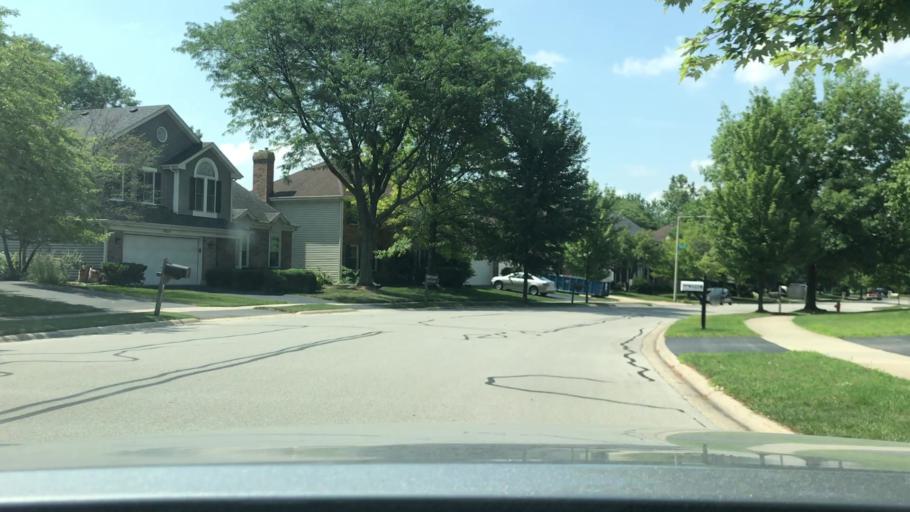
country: US
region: Illinois
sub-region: DuPage County
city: Woodridge
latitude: 41.7372
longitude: -88.0951
